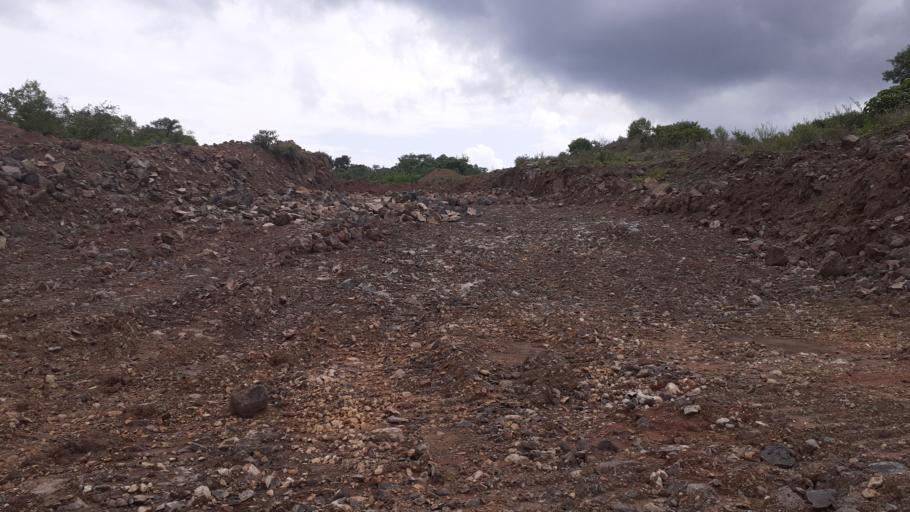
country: ET
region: Southern Nations, Nationalities, and People's Region
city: Areka
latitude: 7.5638
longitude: 37.5103
